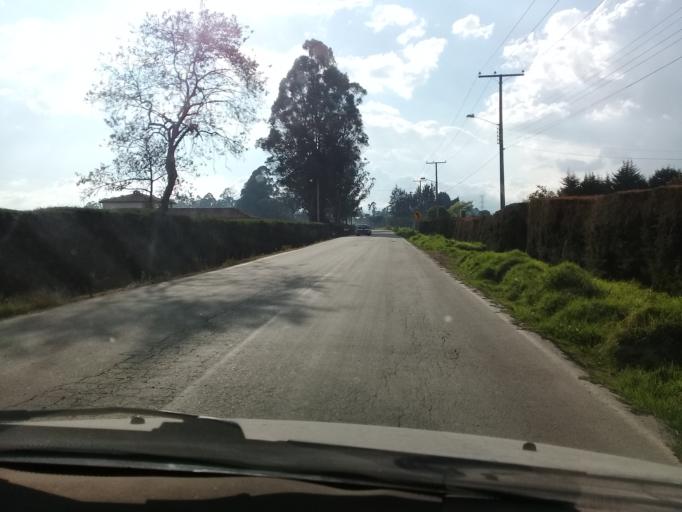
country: CO
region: Cundinamarca
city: El Rosal
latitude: 4.8151
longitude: -74.2565
